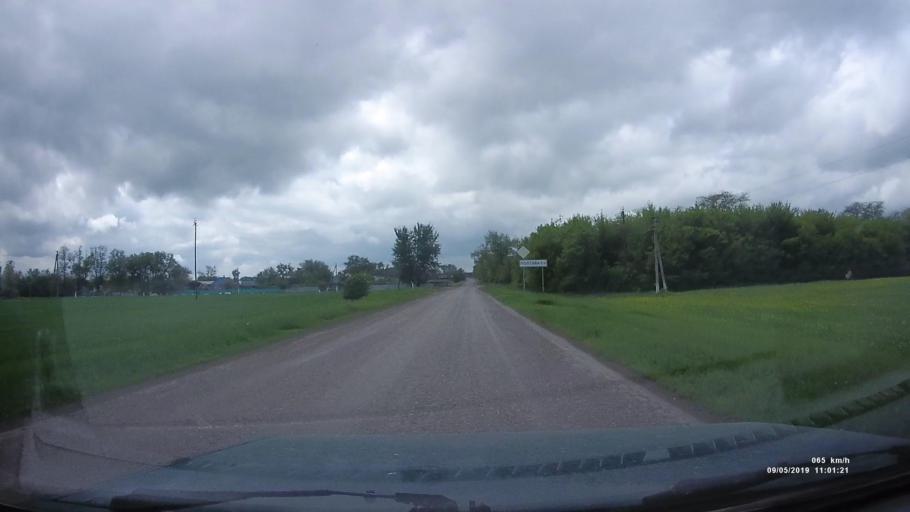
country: RU
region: Rostov
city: Peshkovo
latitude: 46.8498
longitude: 39.2153
